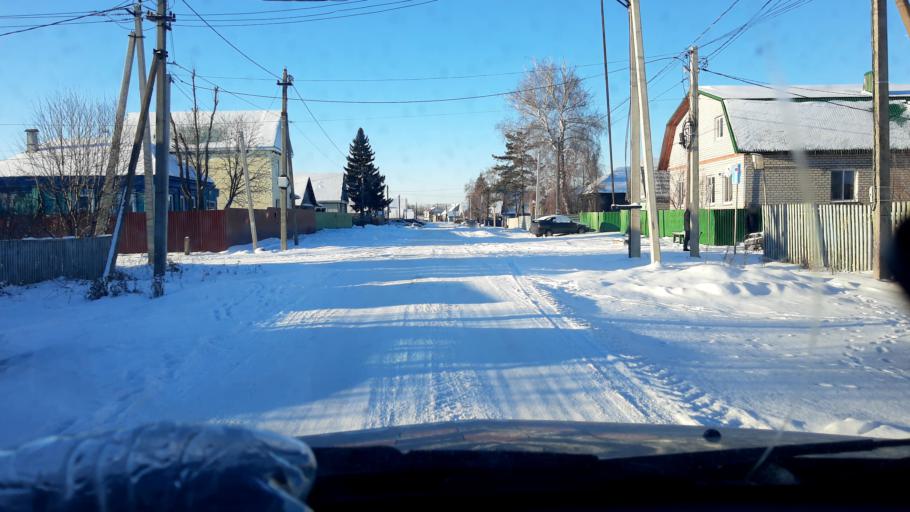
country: RU
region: Bashkortostan
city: Ufa
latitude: 54.6171
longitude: 55.9423
